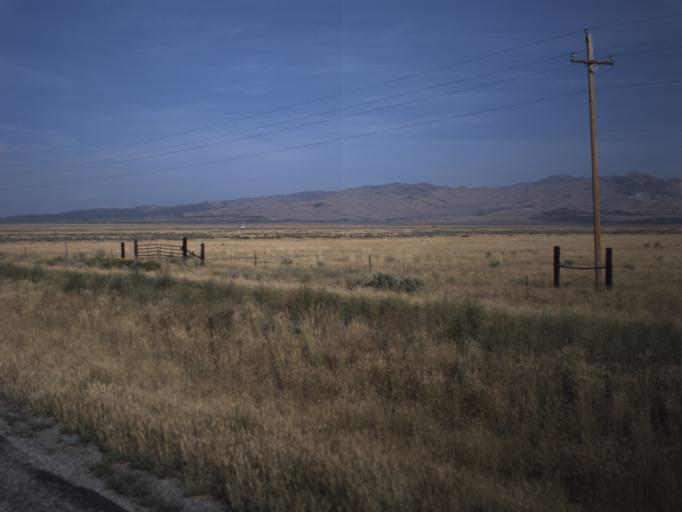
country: US
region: Idaho
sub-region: Oneida County
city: Malad City
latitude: 41.9663
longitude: -112.9492
